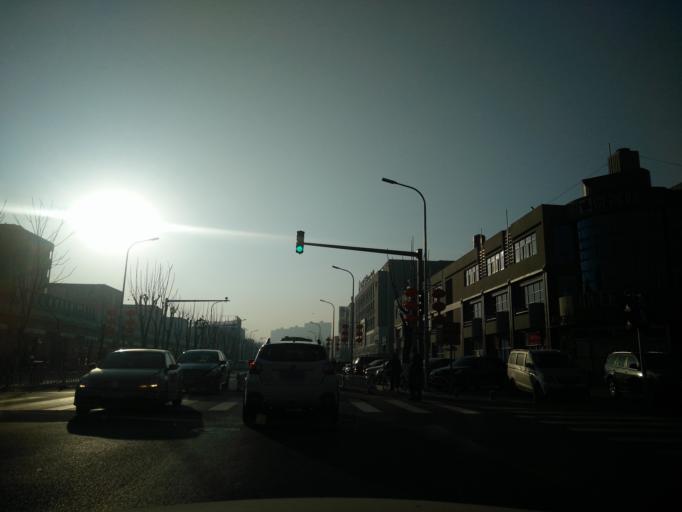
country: CN
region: Beijing
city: Jiugong
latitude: 39.7948
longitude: 116.4735
